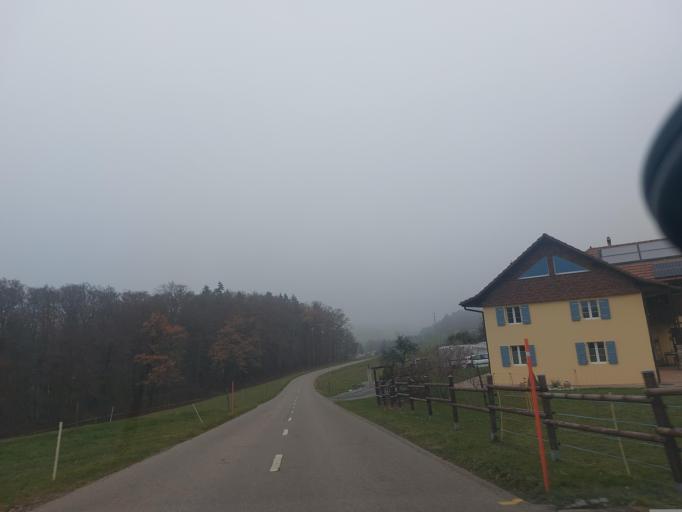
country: CH
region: Fribourg
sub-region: Veveyse District
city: Chatel-Saint-Denis
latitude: 46.5711
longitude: 6.8823
